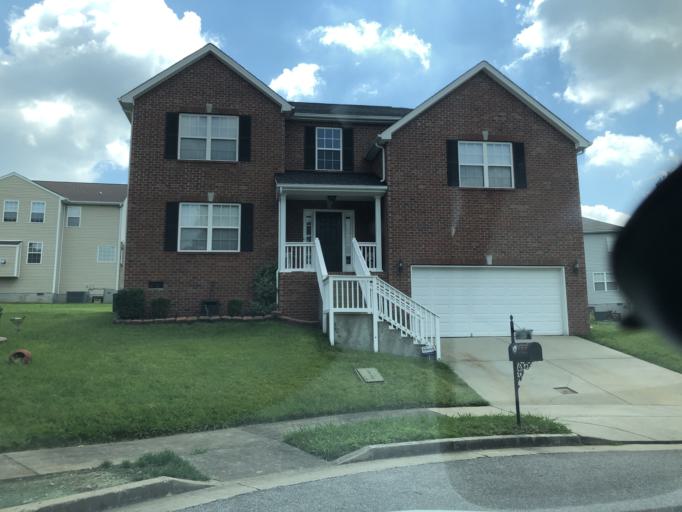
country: US
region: Tennessee
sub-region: Rutherford County
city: La Vergne
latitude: 36.0439
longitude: -86.6227
